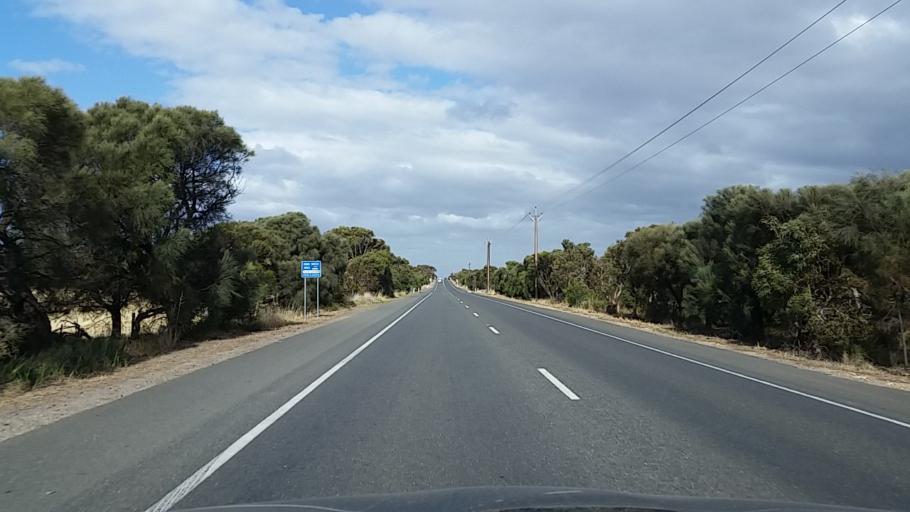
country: AU
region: South Australia
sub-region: Alexandrina
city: Goolwa
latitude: -35.5062
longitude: 138.7597
